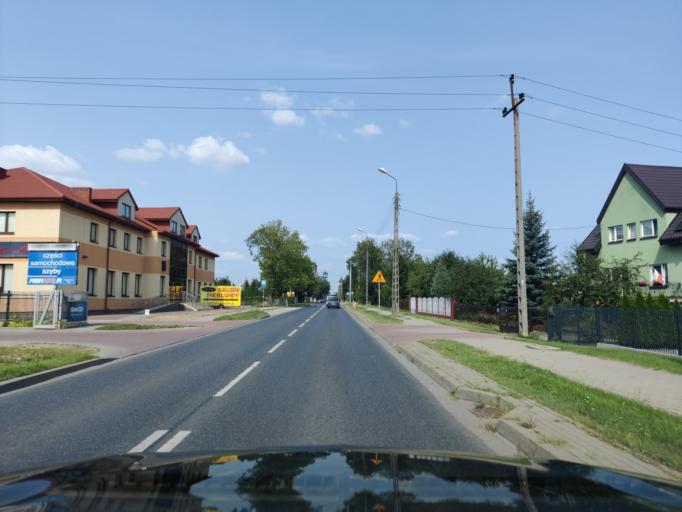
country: PL
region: Masovian Voivodeship
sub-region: Powiat pultuski
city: Pultusk
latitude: 52.7210
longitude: 21.0861
